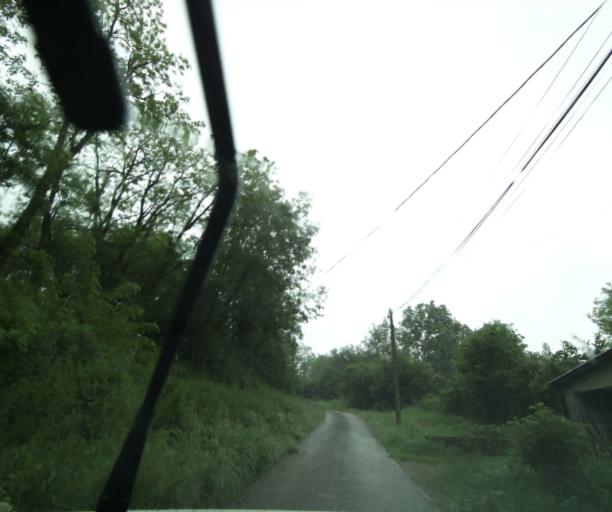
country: FR
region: Bourgogne
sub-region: Departement de Saone-et-Loire
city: Matour
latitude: 46.3690
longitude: 4.3885
